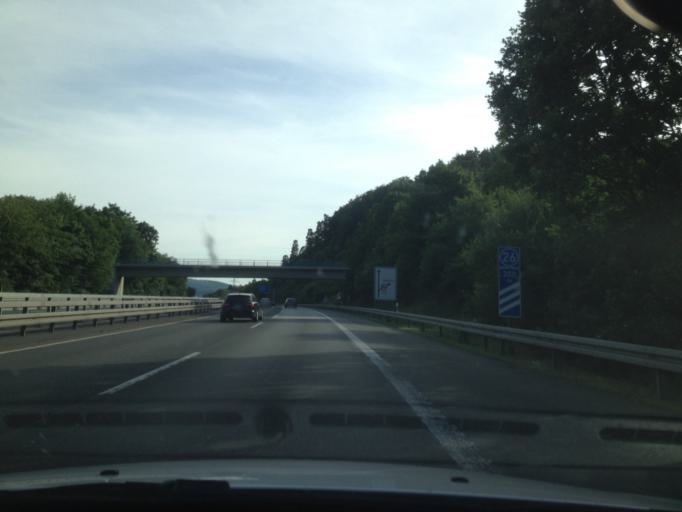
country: DE
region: Hesse
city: Herborn
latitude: 50.6847
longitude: 8.2876
